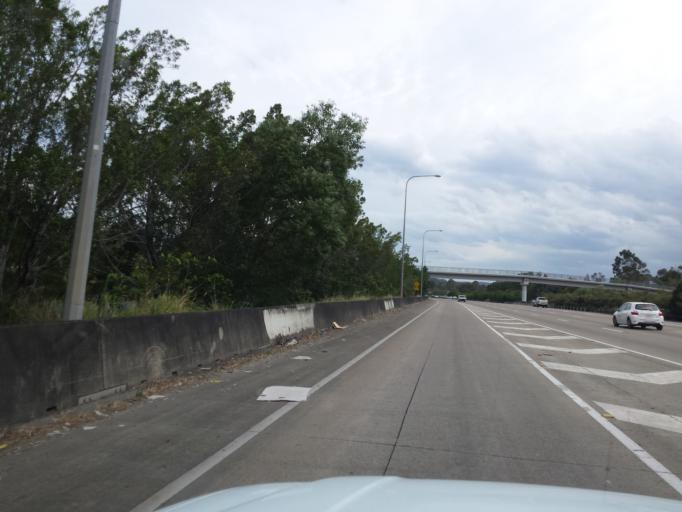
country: AU
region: Queensland
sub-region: Gold Coast
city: Oxenford
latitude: -27.8885
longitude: 153.3155
